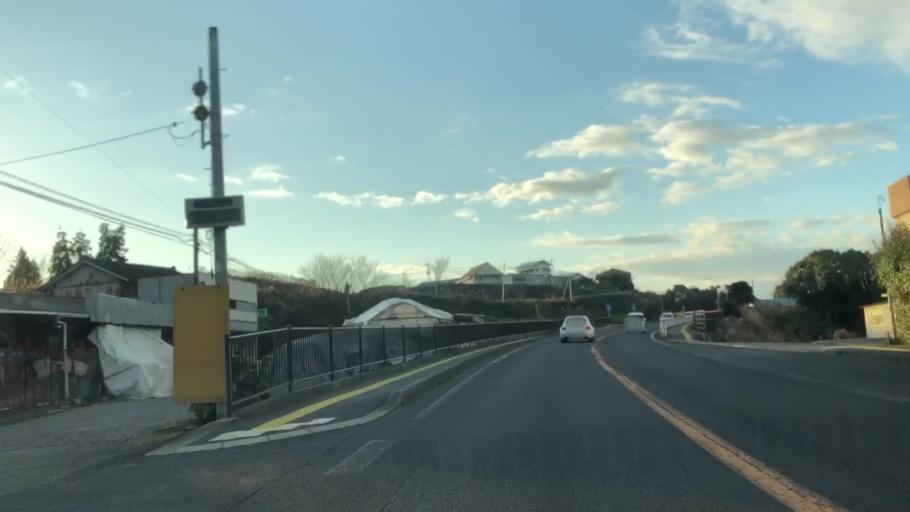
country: JP
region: Oita
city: Bungo-Takada-shi
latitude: 33.5352
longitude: 131.3137
